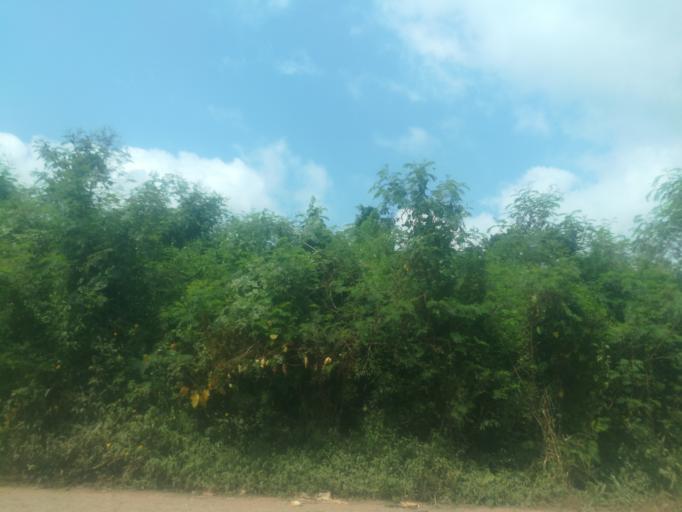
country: NG
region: Oyo
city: Moniya
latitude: 7.5699
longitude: 3.9103
